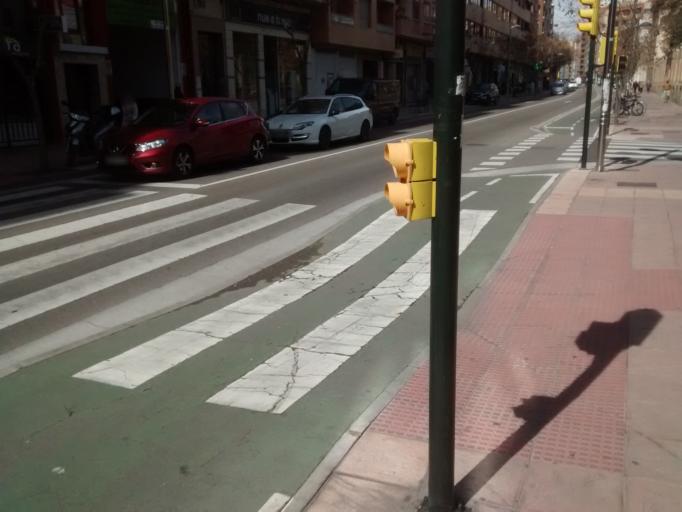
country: ES
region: Aragon
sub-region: Provincia de Zaragoza
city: Zaragoza
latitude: 41.6435
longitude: -0.8696
